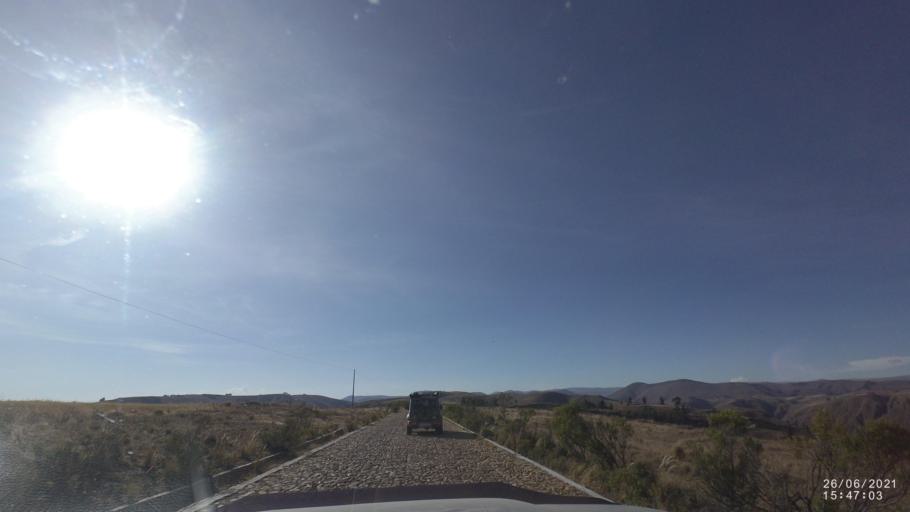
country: BO
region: Cochabamba
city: Arani
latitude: -17.8728
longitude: -65.6984
